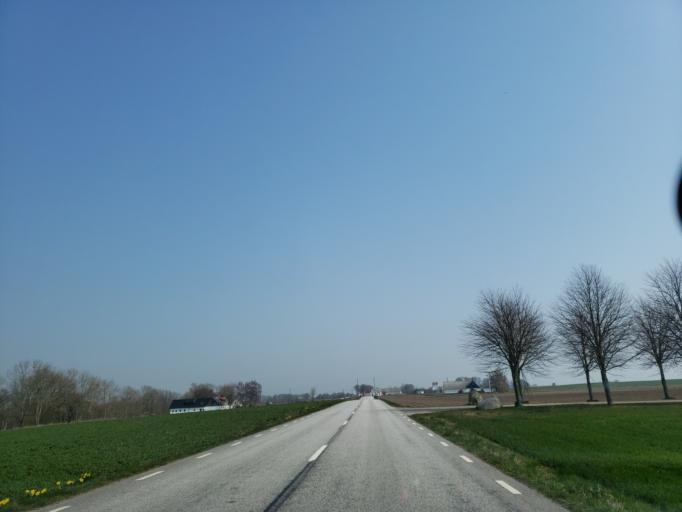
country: SE
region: Skane
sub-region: Simrishamns Kommun
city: Simrishamn
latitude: 55.4687
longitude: 14.2174
